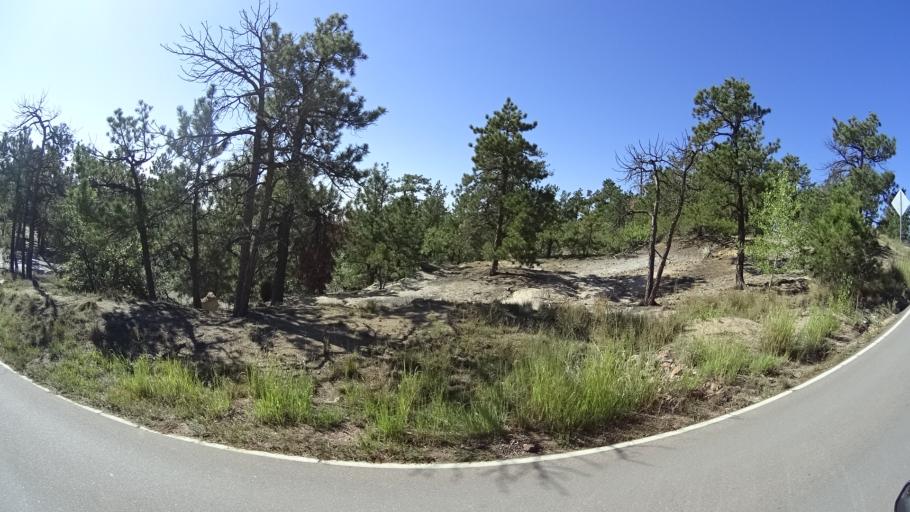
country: US
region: Colorado
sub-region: El Paso County
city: Cimarron Hills
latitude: 38.8773
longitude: -104.7661
